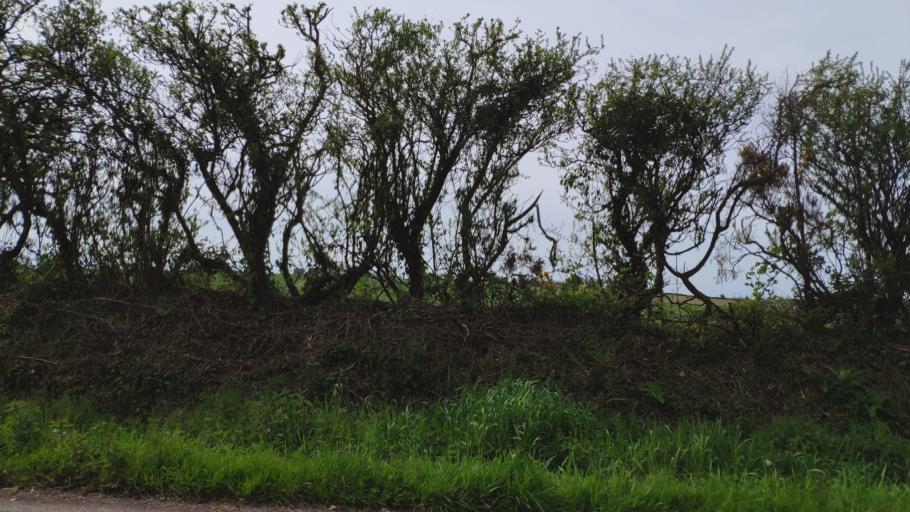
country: IE
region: Munster
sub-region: County Cork
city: Blarney
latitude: 51.9913
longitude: -8.5030
